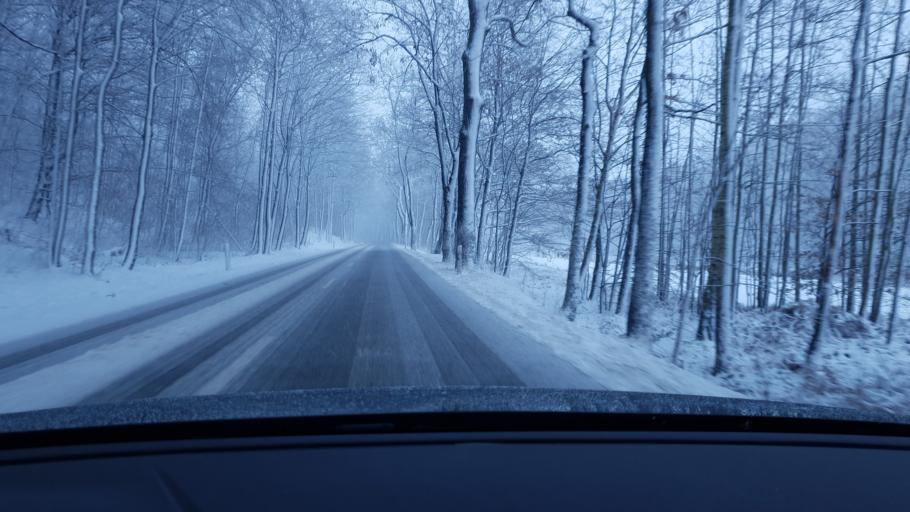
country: DE
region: Saxony
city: Claussnitz
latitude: 50.9168
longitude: 12.8829
